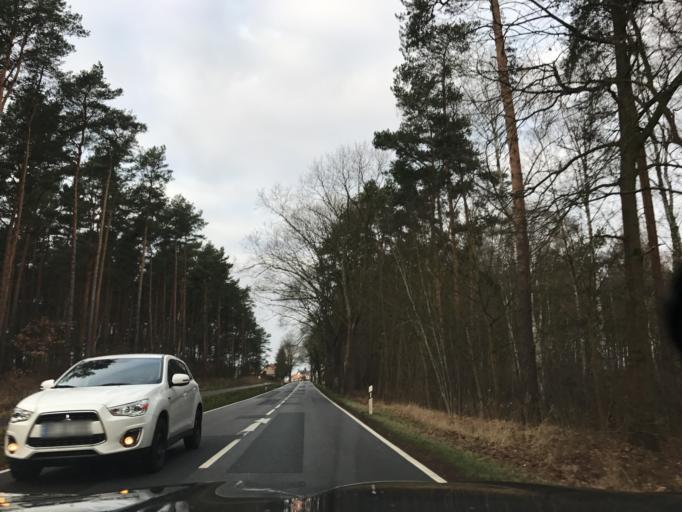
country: DE
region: Brandenburg
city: Golzow
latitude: 52.3462
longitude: 12.6378
